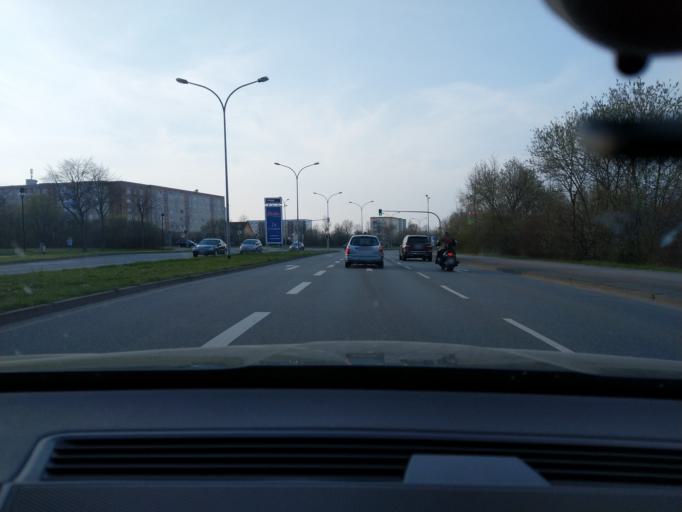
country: DE
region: Mecklenburg-Vorpommern
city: Stralsund
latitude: 54.3101
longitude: 13.0447
